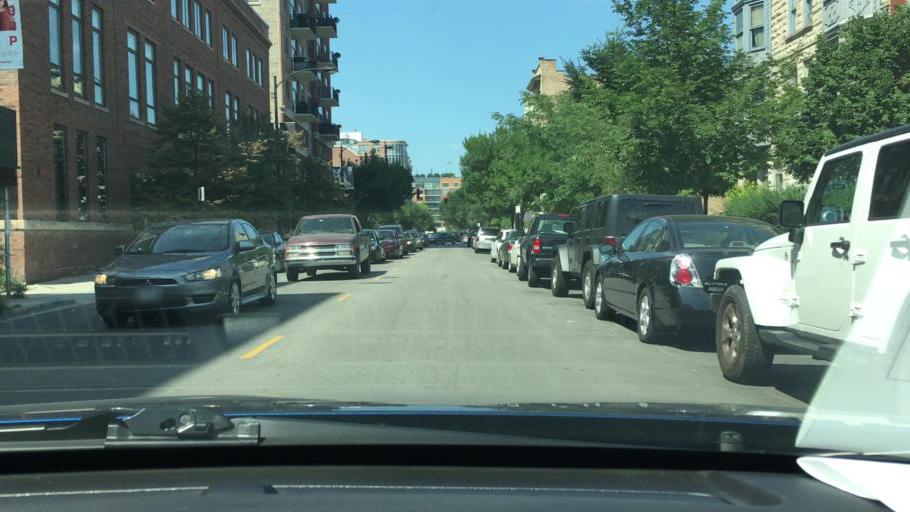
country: US
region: Illinois
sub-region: Cook County
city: Chicago
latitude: 41.8781
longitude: -87.6570
